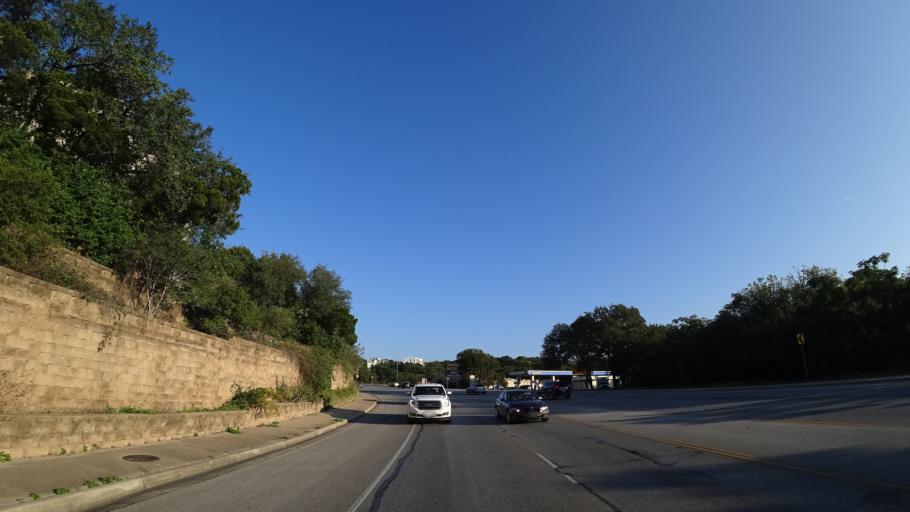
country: US
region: Texas
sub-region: Travis County
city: Rollingwood
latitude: 30.2698
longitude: -97.7862
